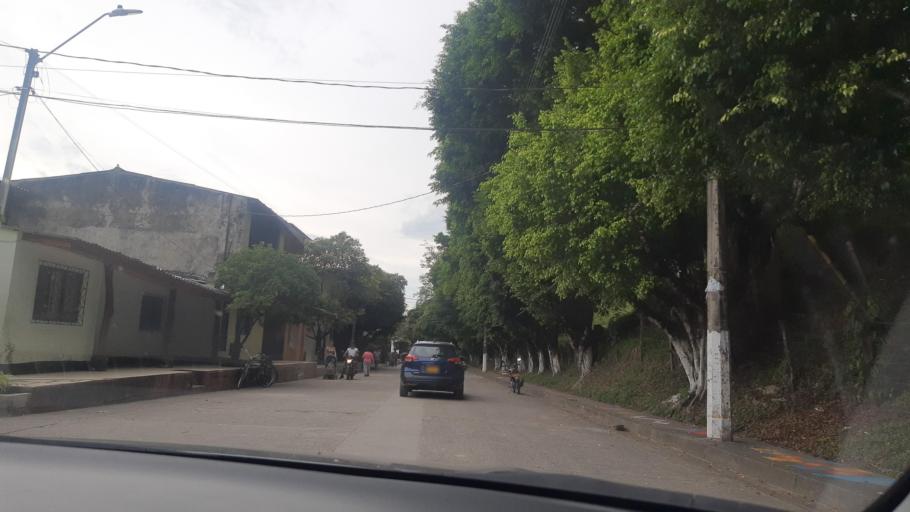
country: CO
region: Antioquia
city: Puerto Triunfo
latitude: 5.8717
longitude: -74.6409
